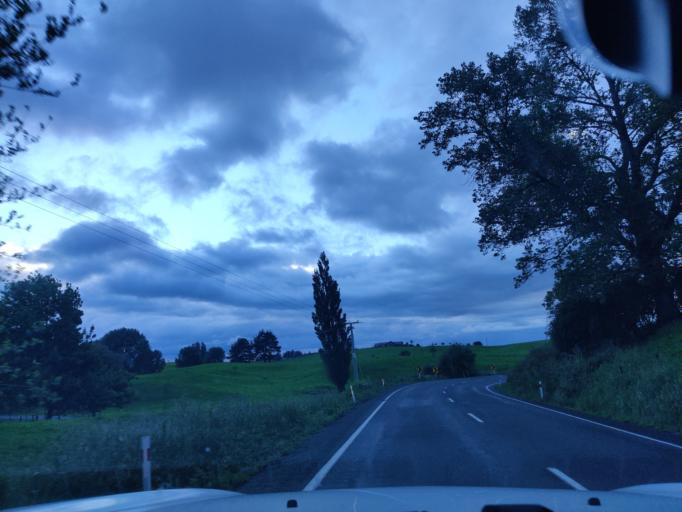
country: NZ
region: Waikato
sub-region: South Waikato District
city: Tokoroa
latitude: -38.1625
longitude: 175.7667
